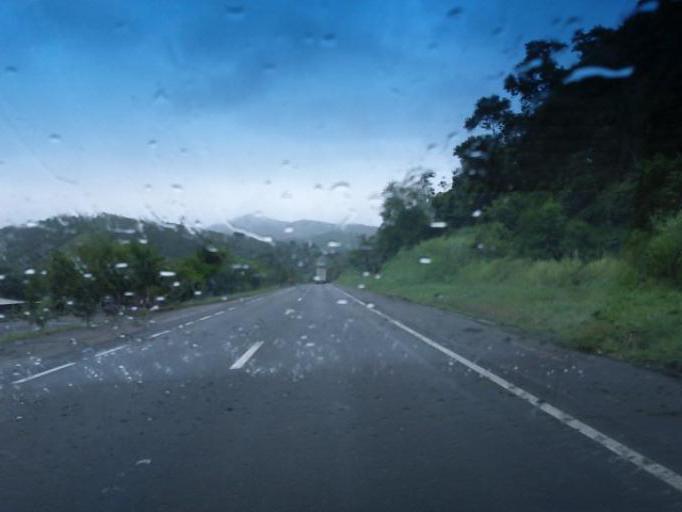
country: BR
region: Sao Paulo
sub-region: Cajati
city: Cajati
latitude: -24.8114
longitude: -48.2107
